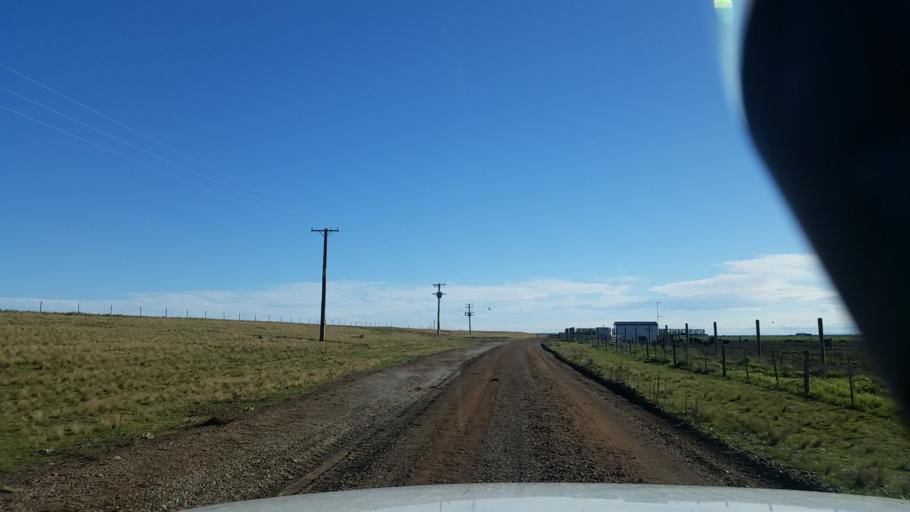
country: NZ
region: Canterbury
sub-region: Selwyn District
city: Lincoln
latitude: -43.8123
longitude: 172.6547
